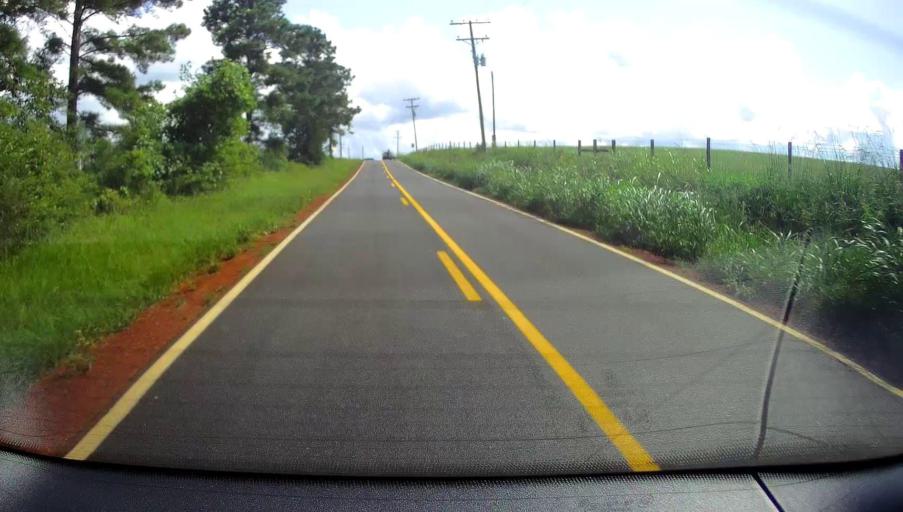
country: US
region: Georgia
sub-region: Upson County
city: Thomaston
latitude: 32.9308
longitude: -84.2906
